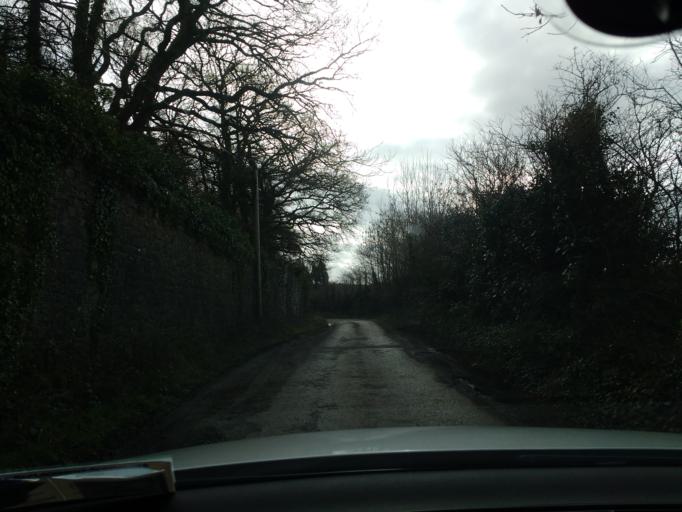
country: IE
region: Leinster
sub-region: Laois
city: Rathdowney
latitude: 52.6636
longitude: -7.5755
